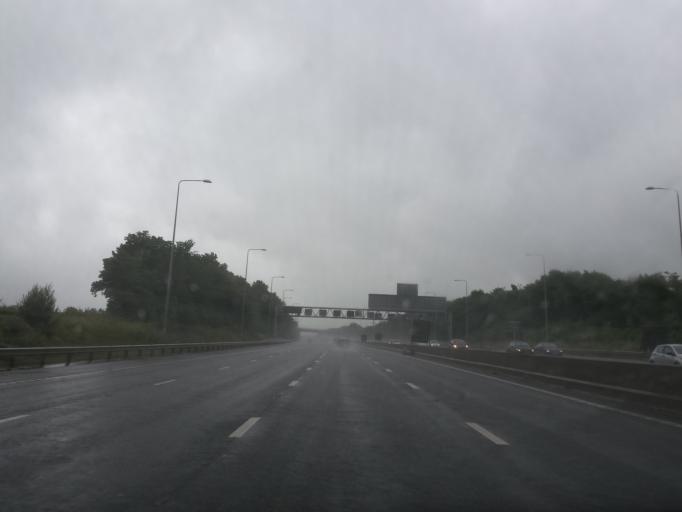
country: GB
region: England
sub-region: Derbyshire
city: Pinxton
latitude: 53.0848
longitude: -1.2998
